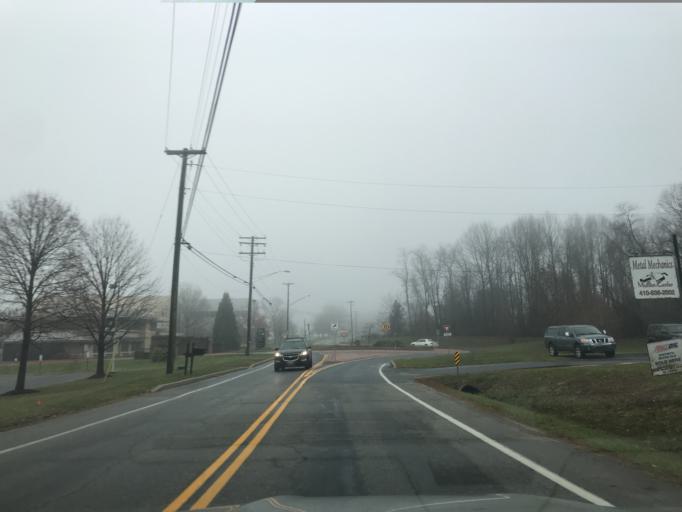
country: US
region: Maryland
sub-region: Harford County
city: South Bel Air
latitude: 39.5624
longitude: -76.2872
